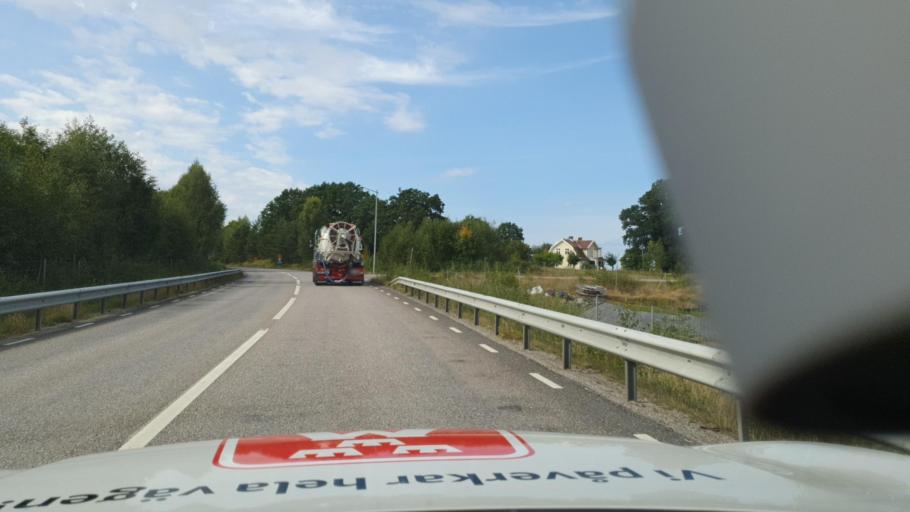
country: SE
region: Vaestra Goetaland
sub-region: Marks Kommun
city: Kinna
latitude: 57.4804
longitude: 12.6871
